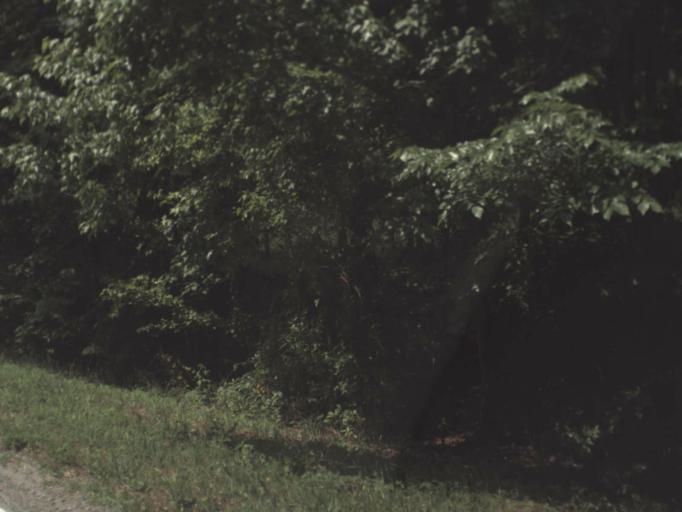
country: US
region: Florida
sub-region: Duval County
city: Jacksonville
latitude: 30.3768
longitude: -81.7649
